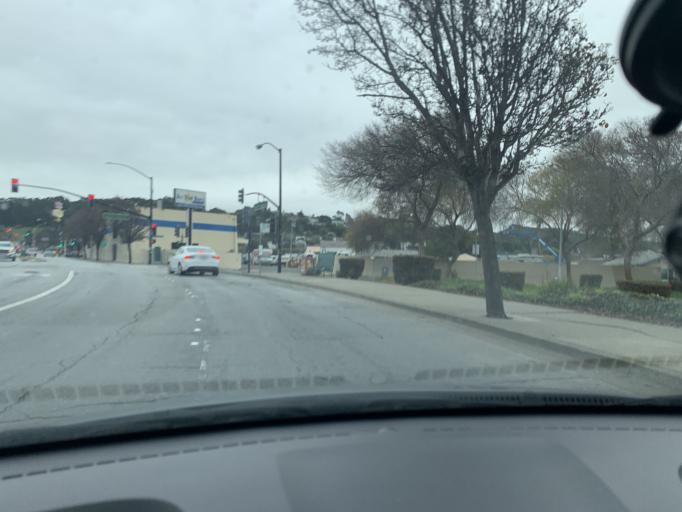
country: US
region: California
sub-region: Contra Costa County
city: Rollingwood
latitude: 37.9537
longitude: -122.3321
